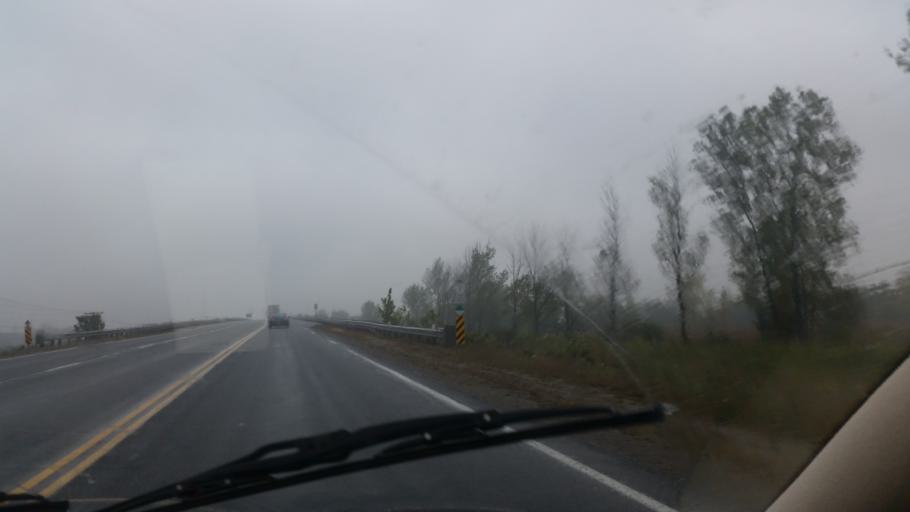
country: CA
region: Ontario
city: Stratford
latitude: 43.2317
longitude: -81.1315
